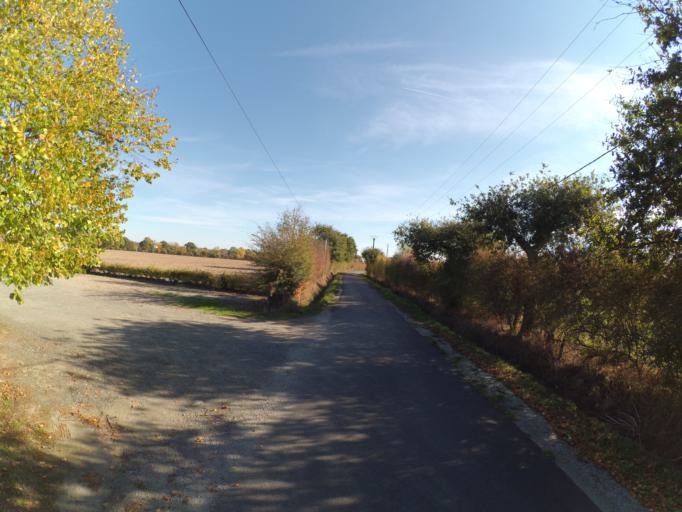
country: FR
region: Pays de la Loire
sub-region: Departement de la Loire-Atlantique
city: Saint-Lumine-de-Clisson
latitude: 47.0825
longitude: -1.3284
